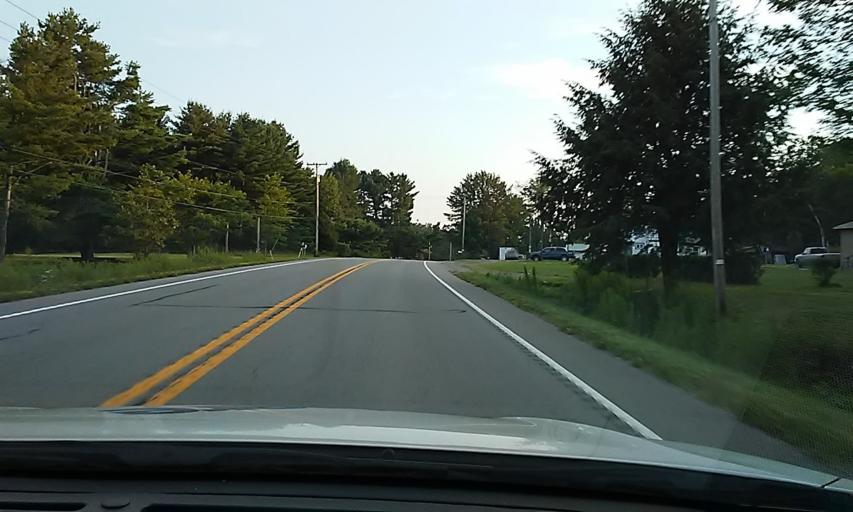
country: US
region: Pennsylvania
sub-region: Forest County
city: Marienville
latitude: 41.4338
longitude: -79.1871
